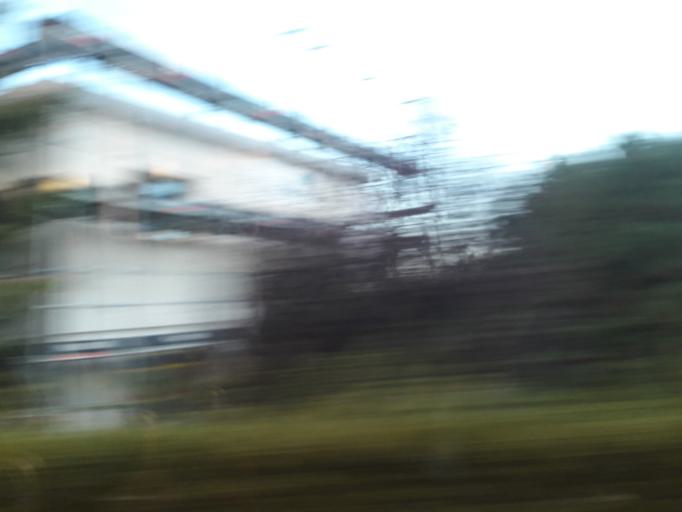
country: CH
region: Solothurn
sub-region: Bezirk Lebern
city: Selzach
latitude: 47.2261
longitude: 7.4677
